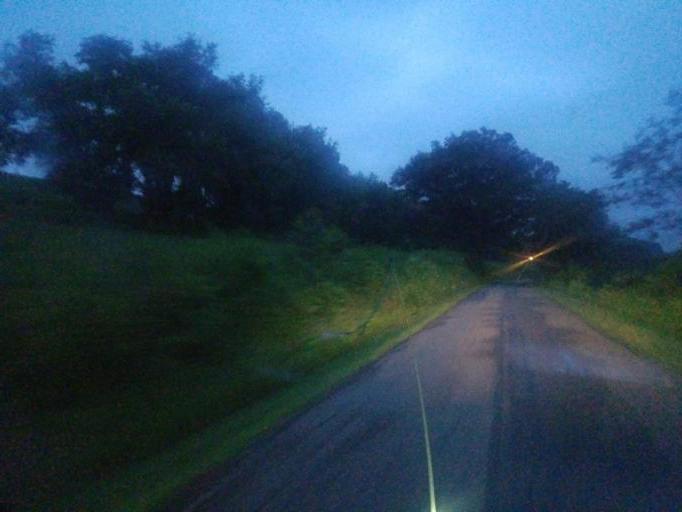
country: US
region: Ohio
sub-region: Carroll County
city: Carrollton
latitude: 40.5672
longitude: -81.0531
